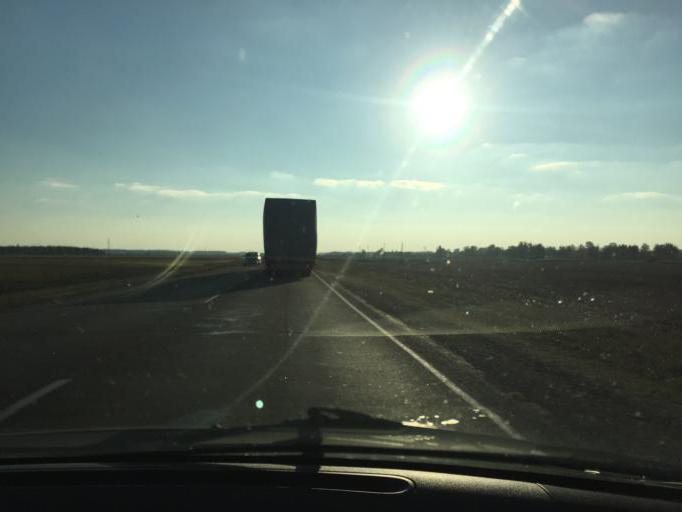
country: BY
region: Brest
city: Asnyezhytsy
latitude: 52.2892
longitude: 26.4155
